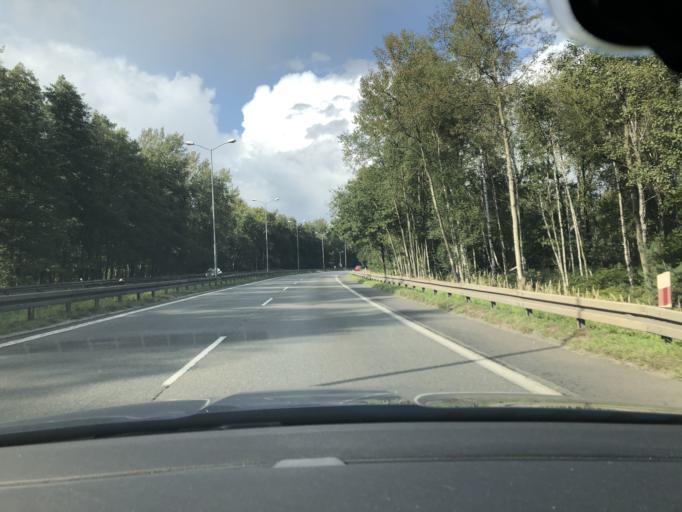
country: PL
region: Silesian Voivodeship
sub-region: Katowice
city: Murcki
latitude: 50.2038
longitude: 19.0511
